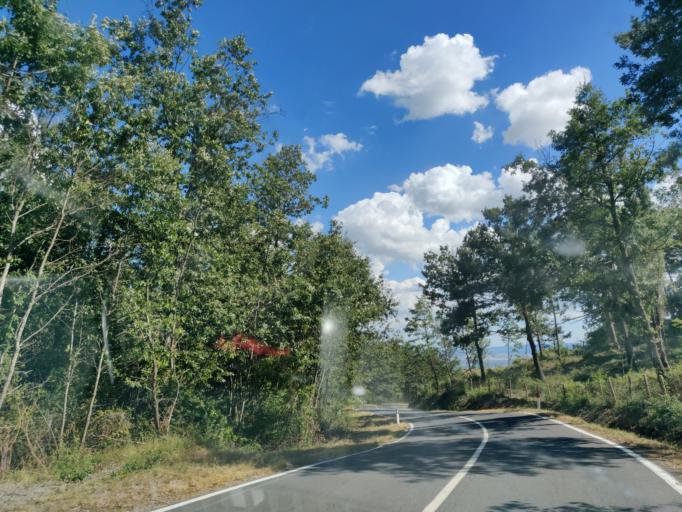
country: IT
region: Tuscany
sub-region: Provincia di Siena
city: Abbadia San Salvatore
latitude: 42.9095
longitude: 11.6927
